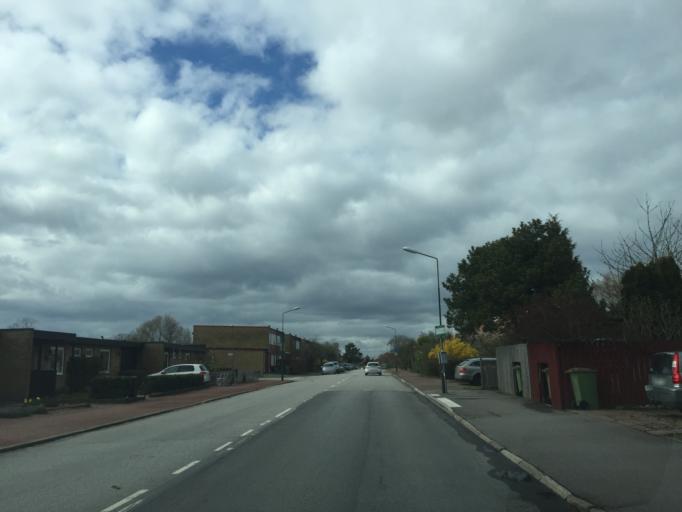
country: SE
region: Skane
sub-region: Malmo
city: Malmoe
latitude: 55.5784
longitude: 12.9638
